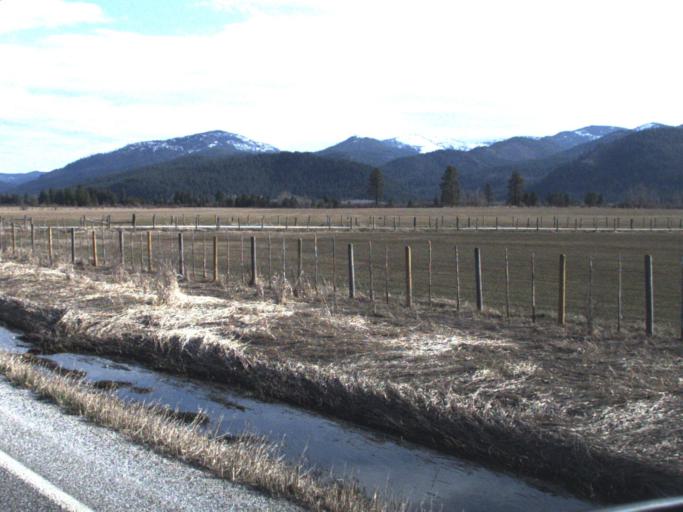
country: US
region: Washington
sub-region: Pend Oreille County
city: Newport
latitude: 48.3608
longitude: -117.3046
